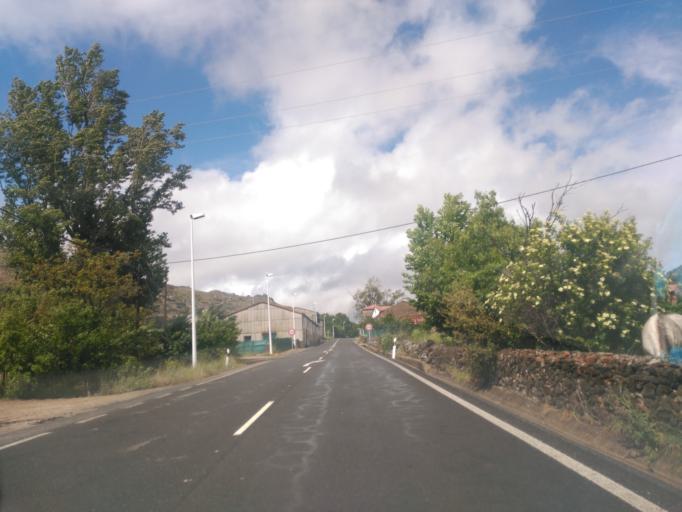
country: ES
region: Castille and Leon
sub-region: Provincia de Salamanca
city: Vallejera de Riofrio
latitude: 40.4079
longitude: -5.7222
